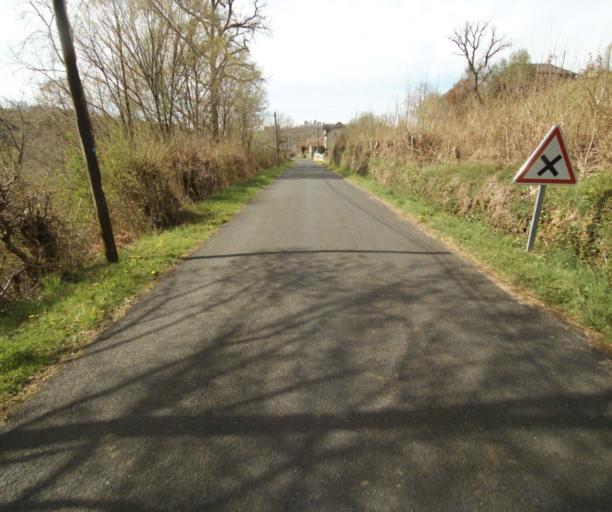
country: FR
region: Limousin
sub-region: Departement de la Correze
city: Laguenne
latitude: 45.2476
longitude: 1.8135
